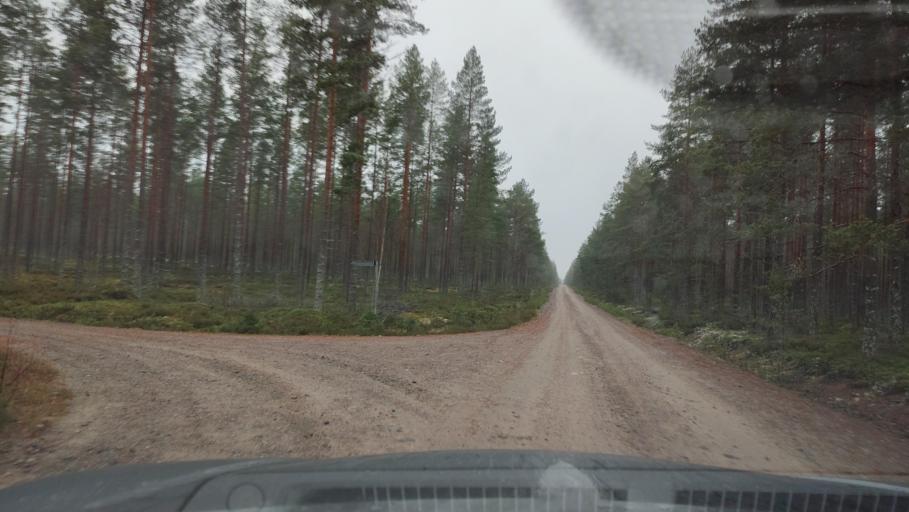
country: FI
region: Southern Ostrobothnia
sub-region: Suupohja
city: Karijoki
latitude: 62.1940
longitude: 21.7434
